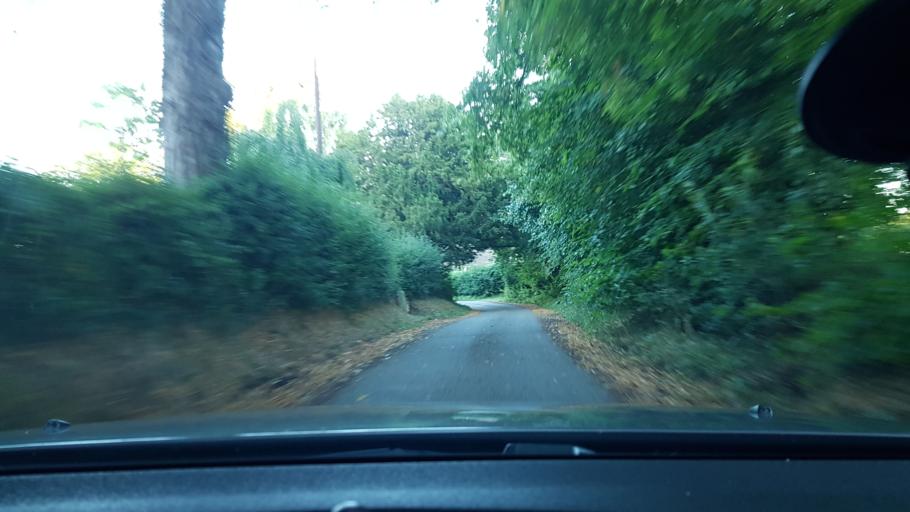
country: GB
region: England
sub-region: Wiltshire
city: Shalbourne
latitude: 51.3870
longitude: -1.5499
